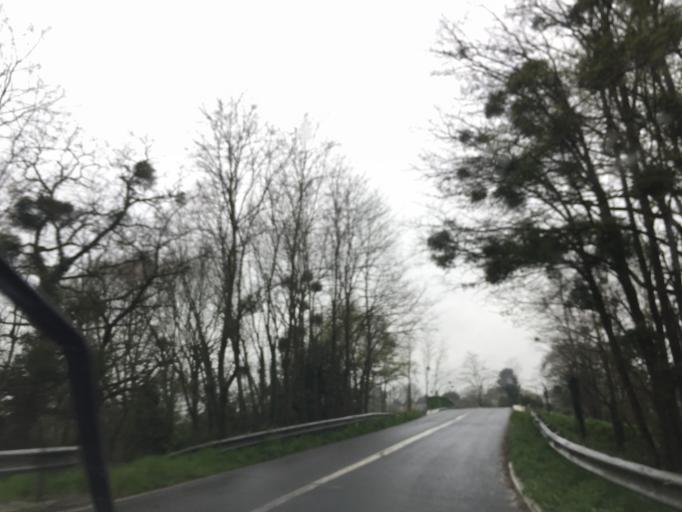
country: FR
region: Pays de la Loire
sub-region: Departement de la Loire-Atlantique
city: Casson
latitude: 47.4106
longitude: -1.5341
